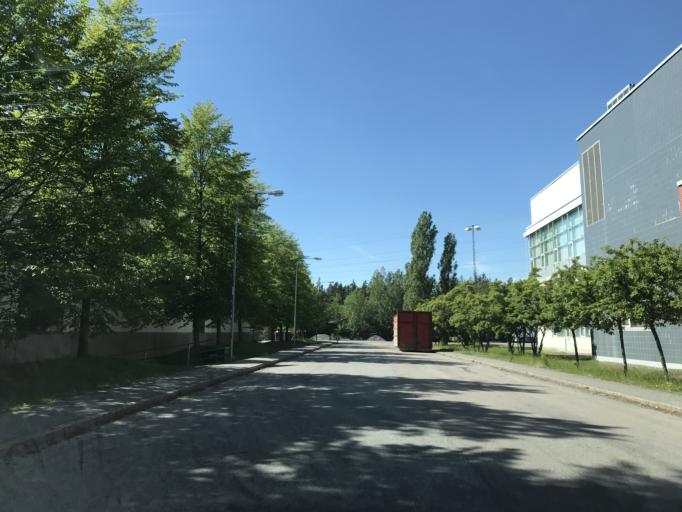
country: SE
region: Stockholm
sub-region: Stockholms Kommun
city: Kista
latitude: 59.4215
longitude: 17.9158
